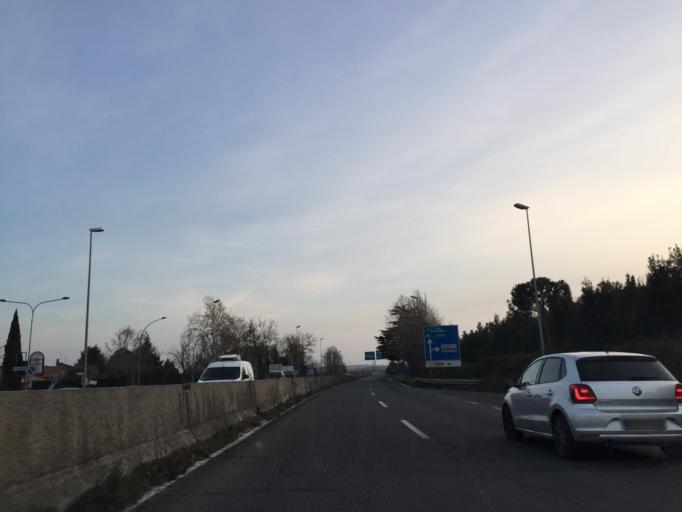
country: IT
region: Latium
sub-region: Citta metropolitana di Roma Capitale
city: Le Rughe
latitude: 42.0613
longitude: 12.3729
